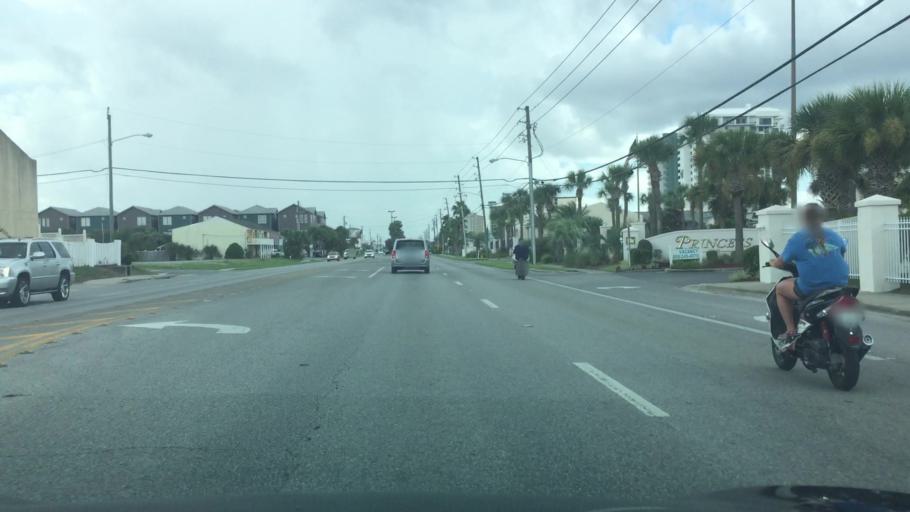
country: US
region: Florida
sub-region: Bay County
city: Lower Grand Lagoon
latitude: 30.1522
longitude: -85.7665
